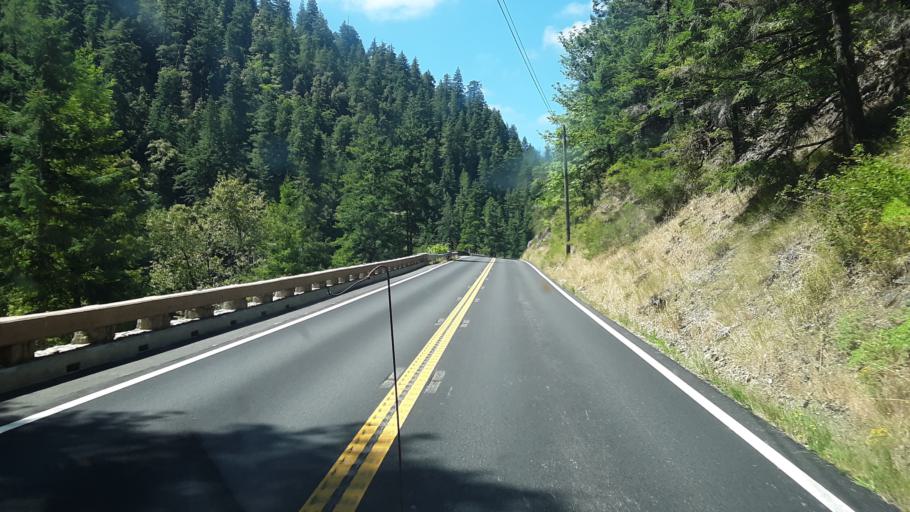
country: US
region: California
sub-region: Del Norte County
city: Bertsch-Oceanview
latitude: 41.8177
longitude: -124.0378
